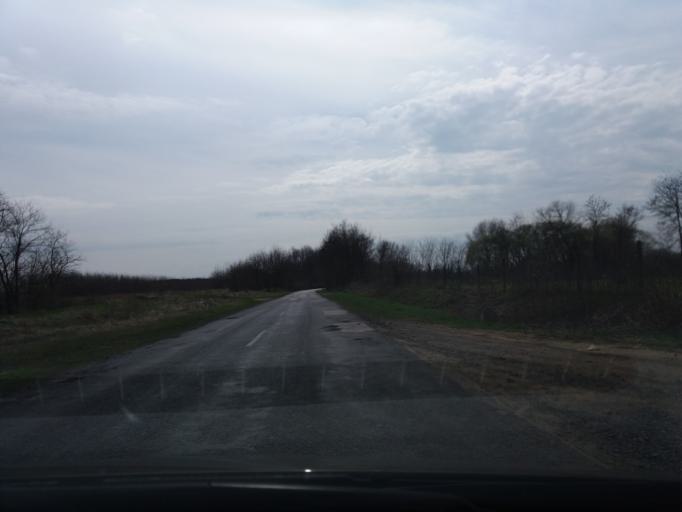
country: HU
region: Szabolcs-Szatmar-Bereg
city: Petnehaza
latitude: 48.0710
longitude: 22.0875
